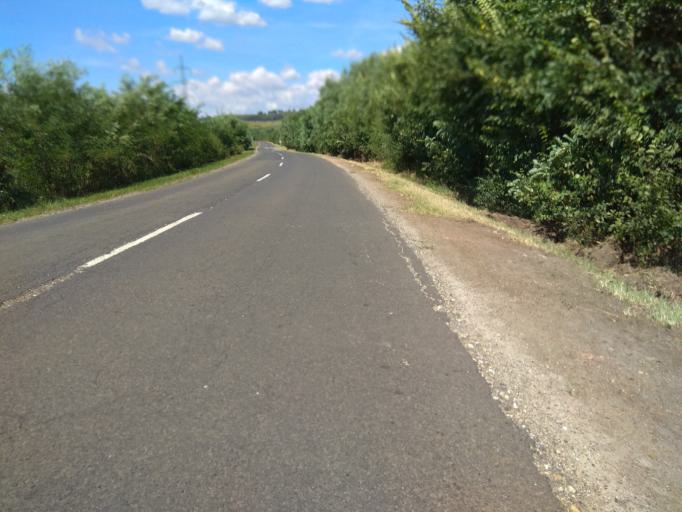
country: HU
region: Borsod-Abauj-Zemplen
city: Sajokaza
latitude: 48.2864
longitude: 20.6186
